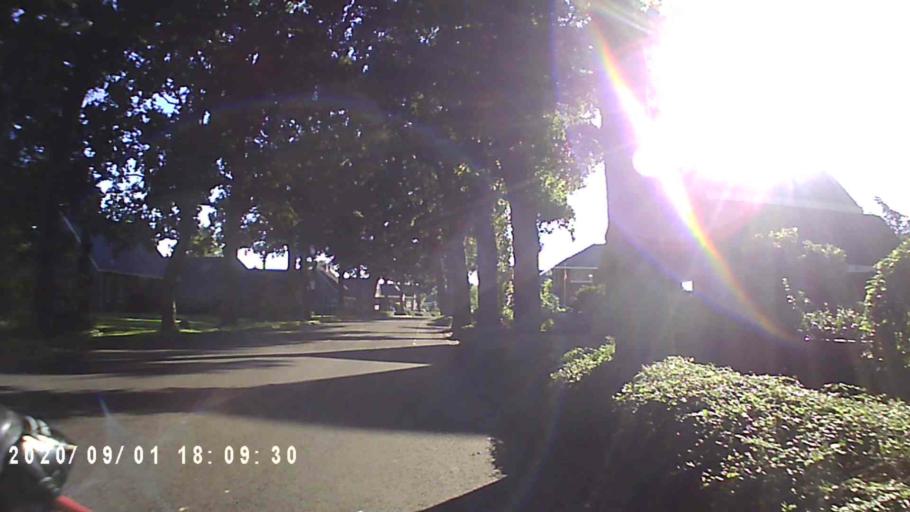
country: NL
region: Groningen
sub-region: Gemeente Hoogezand-Sappemeer
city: Sappemeer
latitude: 53.1939
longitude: 6.7818
